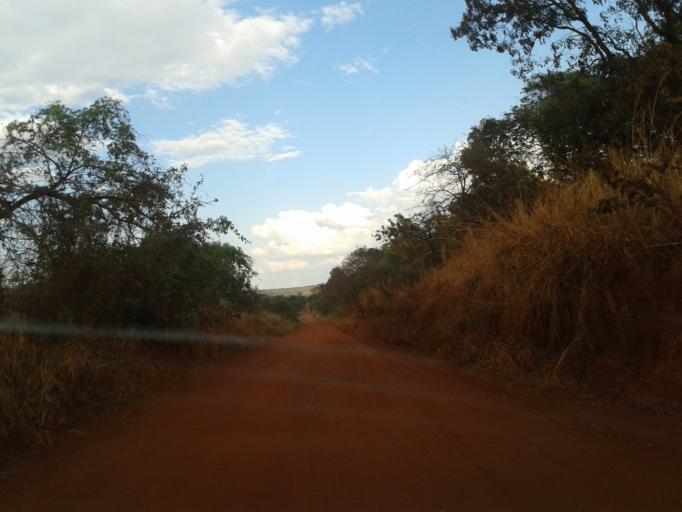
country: BR
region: Minas Gerais
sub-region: Ituiutaba
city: Ituiutaba
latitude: -19.2029
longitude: -49.8120
